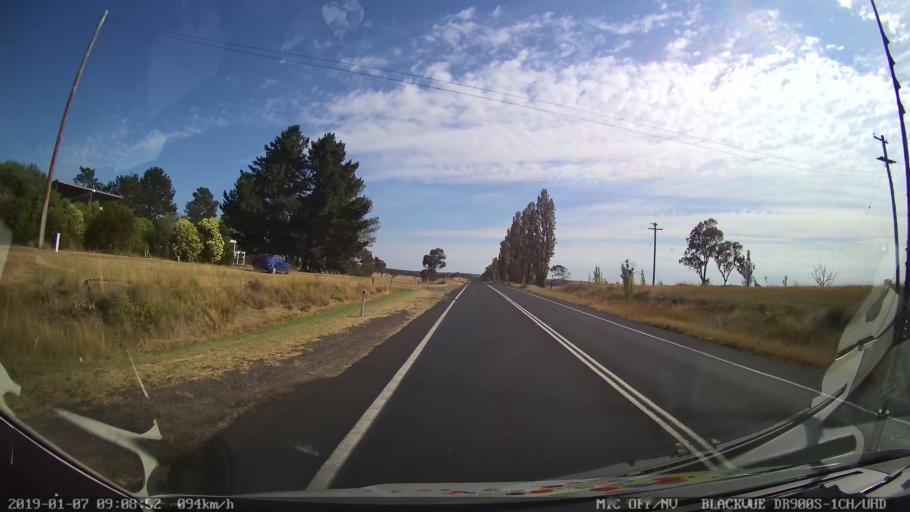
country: AU
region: New South Wales
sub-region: Armidale Dumaresq
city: Armidale
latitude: -30.6658
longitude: 151.4854
